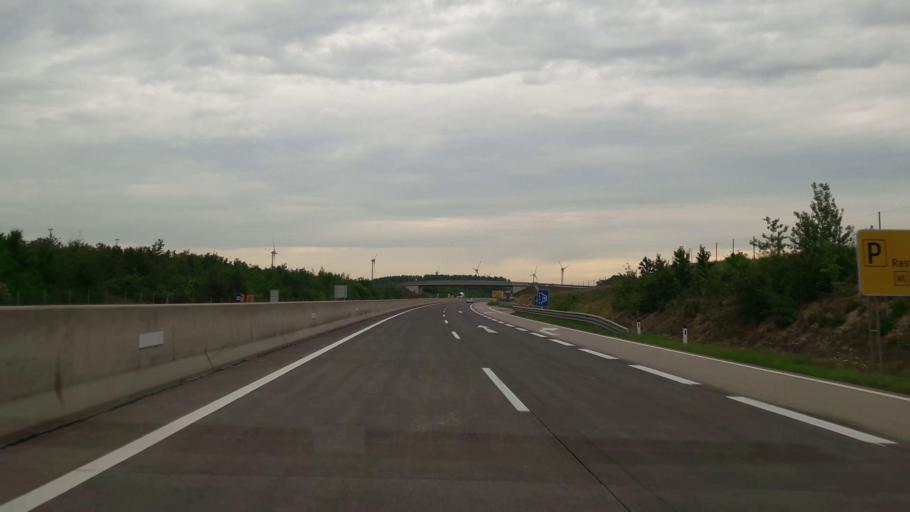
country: AT
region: Burgenland
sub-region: Politischer Bezirk Neusiedl am See
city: Potzneusiedl
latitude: 48.0303
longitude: 16.9609
